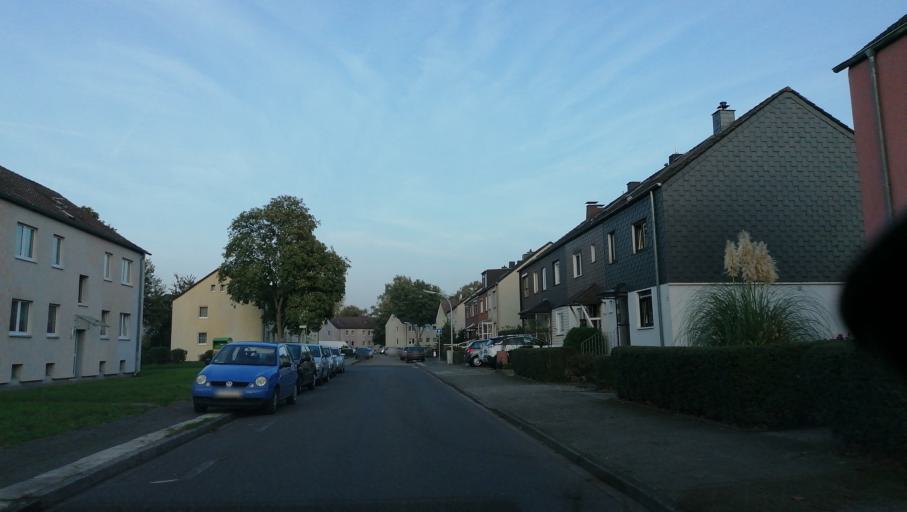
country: DE
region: North Rhine-Westphalia
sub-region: Regierungsbezirk Munster
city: Recklinghausen
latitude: 51.5682
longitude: 7.1827
